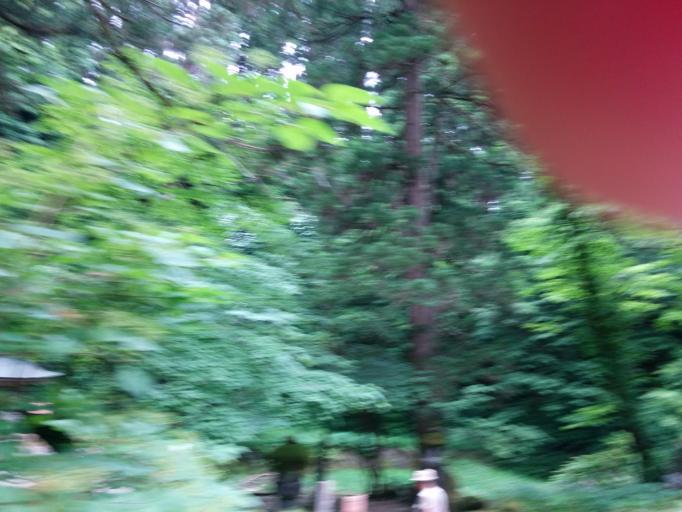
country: JP
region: Yamagata
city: Tsuruoka
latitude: 38.7054
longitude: 139.9663
